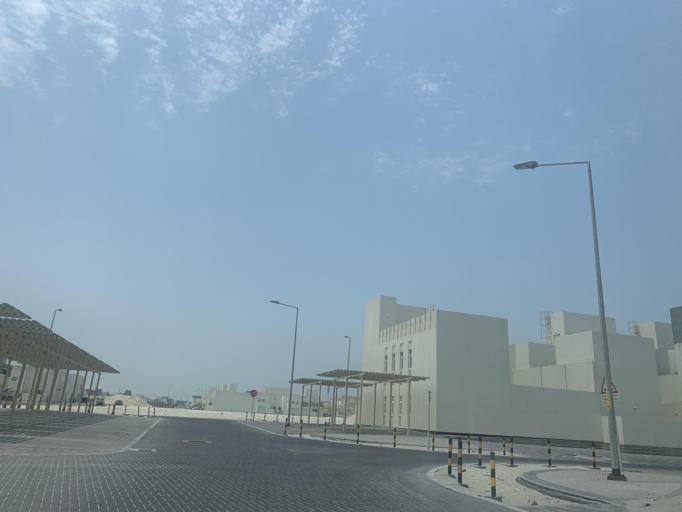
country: BH
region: Muharraq
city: Al Hadd
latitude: 26.2318
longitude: 50.6689
